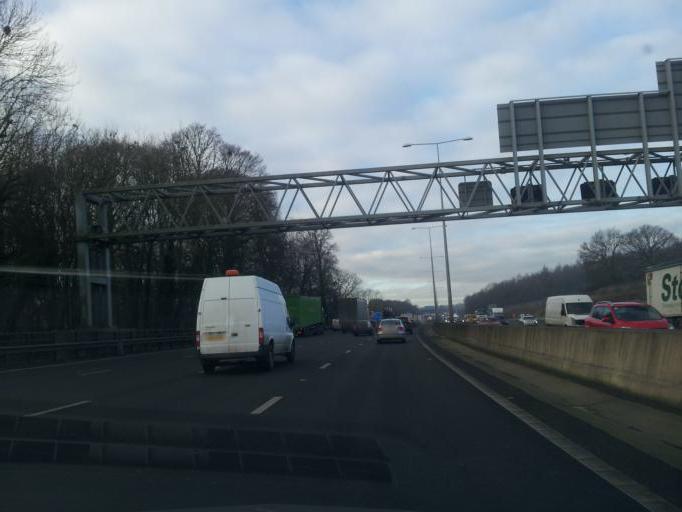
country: GB
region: England
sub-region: Hertfordshire
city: Chorleywood
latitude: 51.6731
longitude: -0.4687
